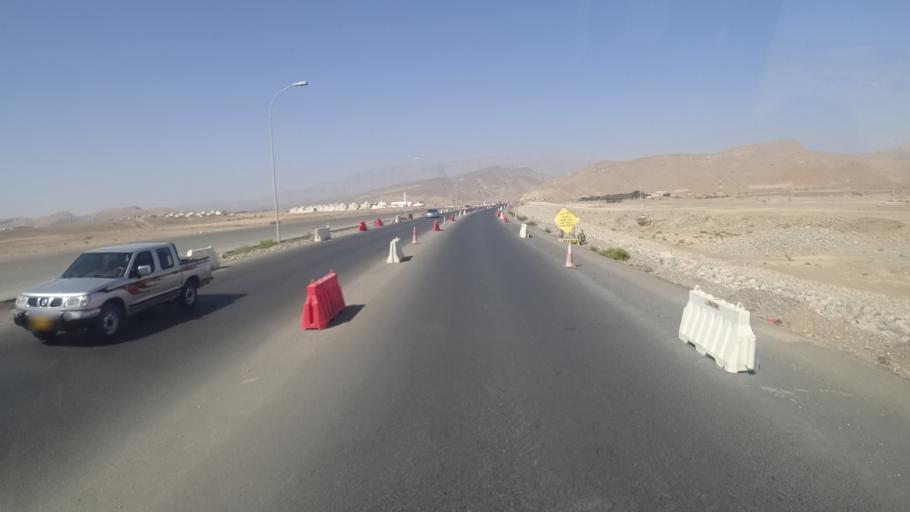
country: OM
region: Ash Sharqiyah
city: Sur
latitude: 22.5172
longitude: 59.4526
